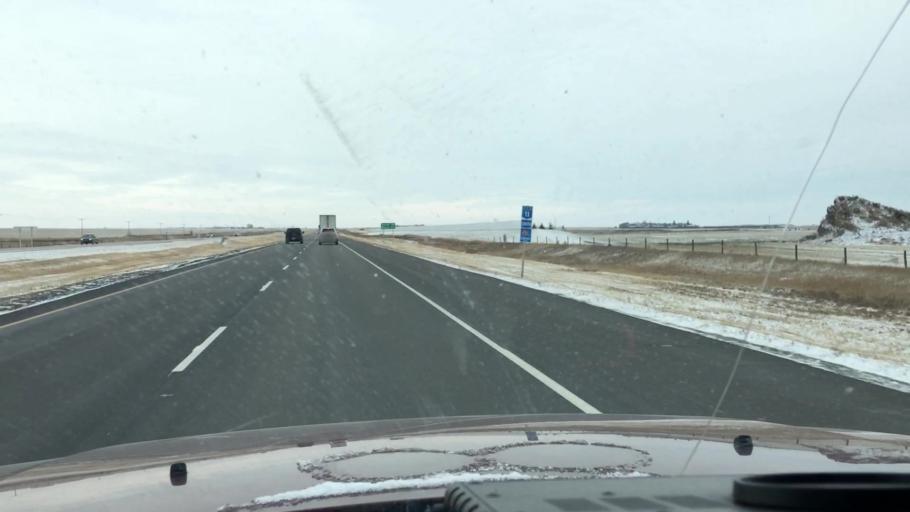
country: CA
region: Saskatchewan
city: Saskatoon
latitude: 51.8084
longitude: -106.4948
